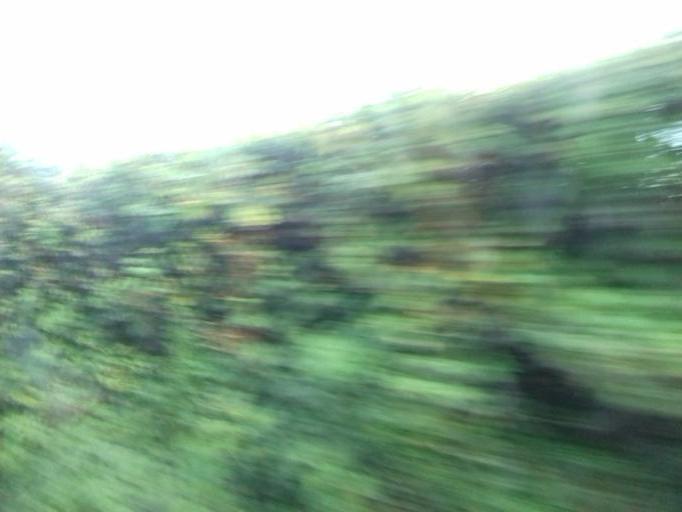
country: IE
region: Leinster
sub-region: Fingal County
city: Swords
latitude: 53.4906
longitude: -6.1993
